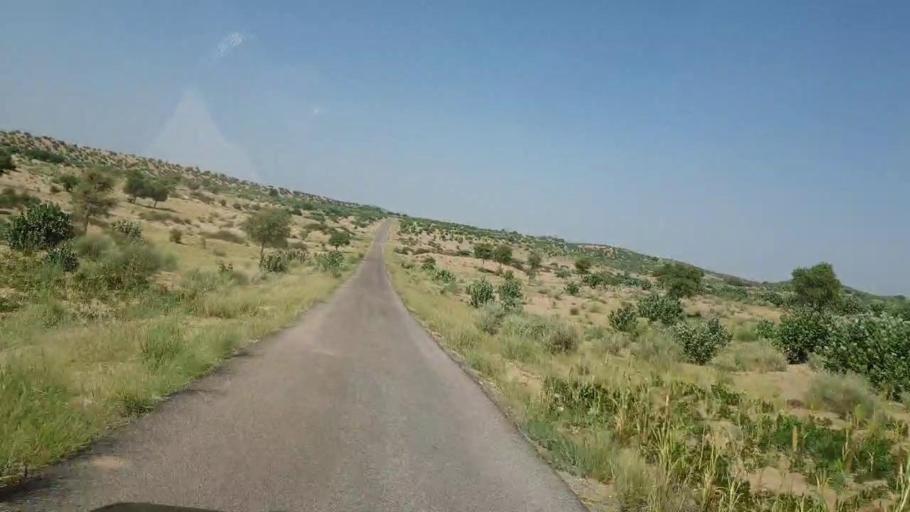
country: PK
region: Sindh
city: Chor
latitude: 25.6347
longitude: 70.3177
